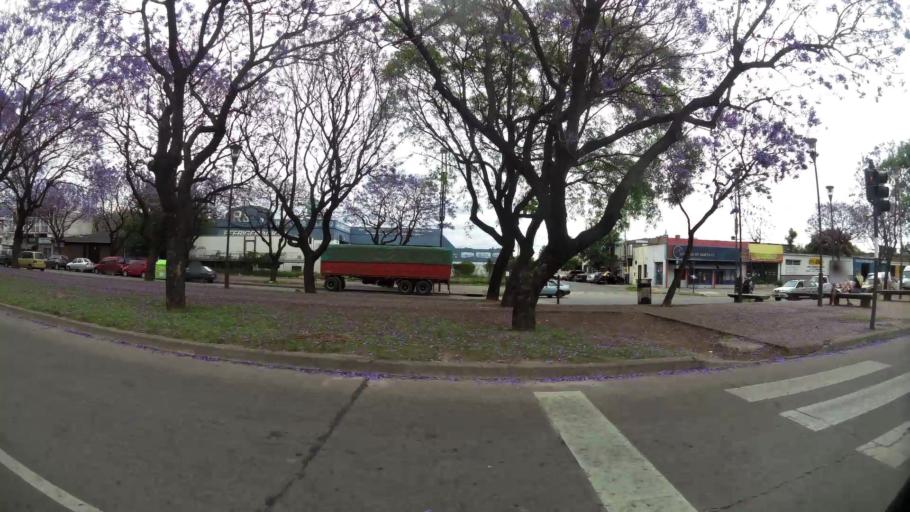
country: AR
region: Santa Fe
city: Gobernador Galvez
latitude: -33.0027
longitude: -60.6650
